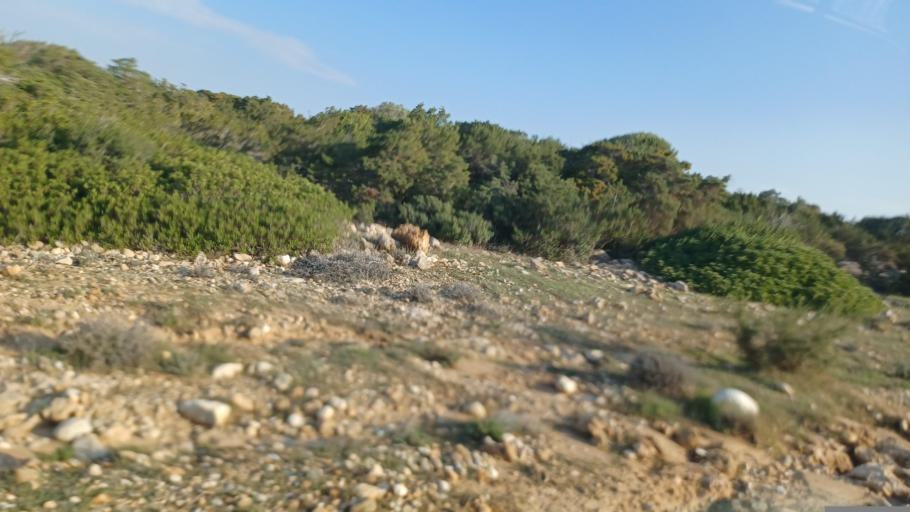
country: CY
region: Pafos
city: Pegeia
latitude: 34.9131
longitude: 32.3305
